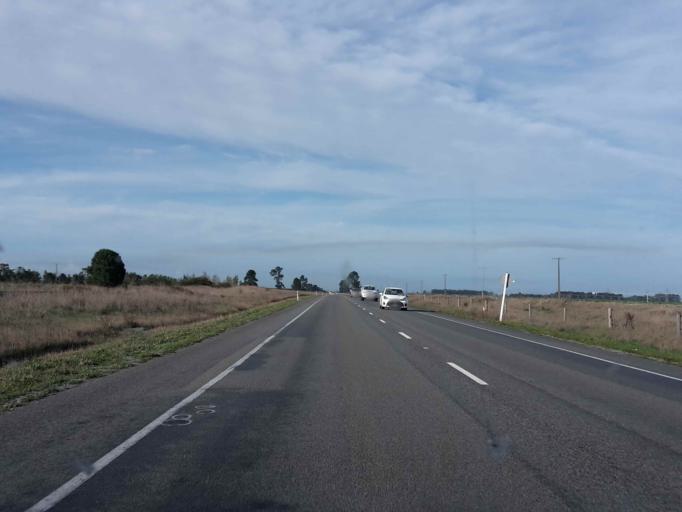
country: NZ
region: Canterbury
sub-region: Ashburton District
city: Tinwald
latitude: -44.0276
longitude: 171.4870
